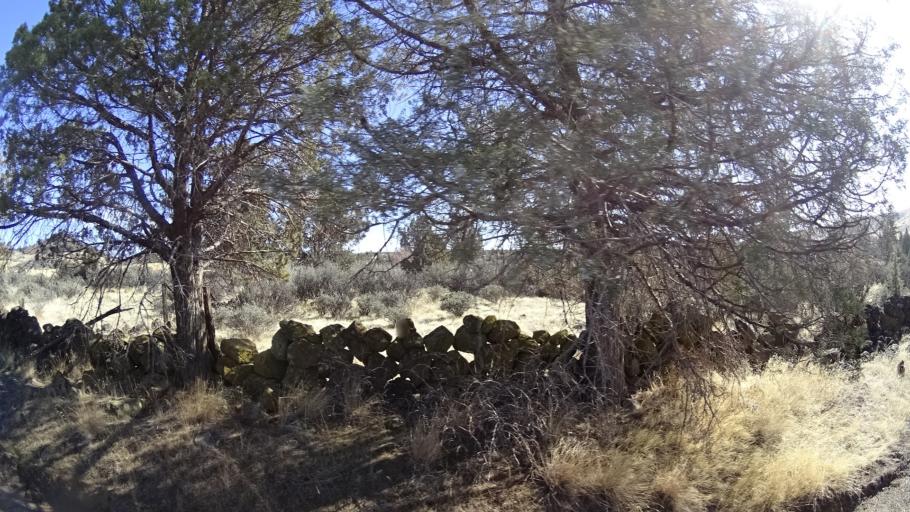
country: US
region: California
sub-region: Siskiyou County
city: Yreka
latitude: 41.7761
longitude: -122.5915
